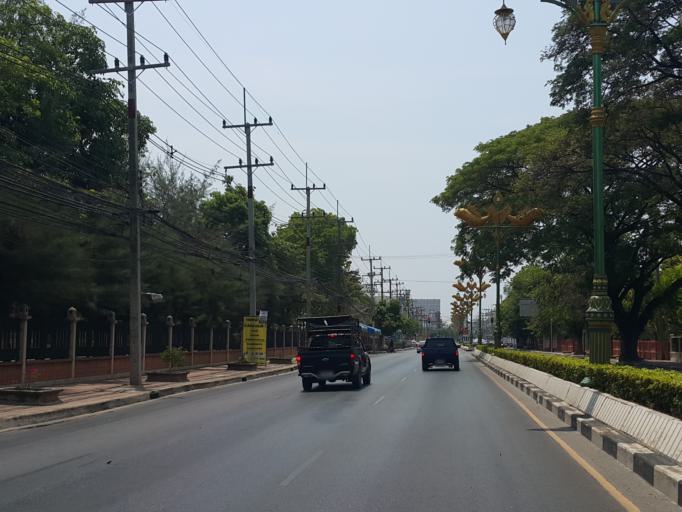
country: TH
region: Kanchanaburi
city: Kanchanaburi
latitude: 14.0318
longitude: 99.5262
